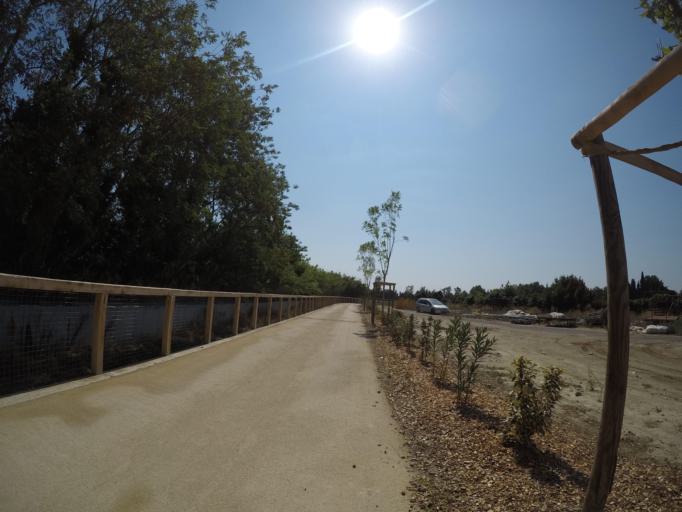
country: FR
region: Languedoc-Roussillon
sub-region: Departement des Pyrenees-Orientales
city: Saint-Esteve
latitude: 42.7023
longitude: 2.8556
